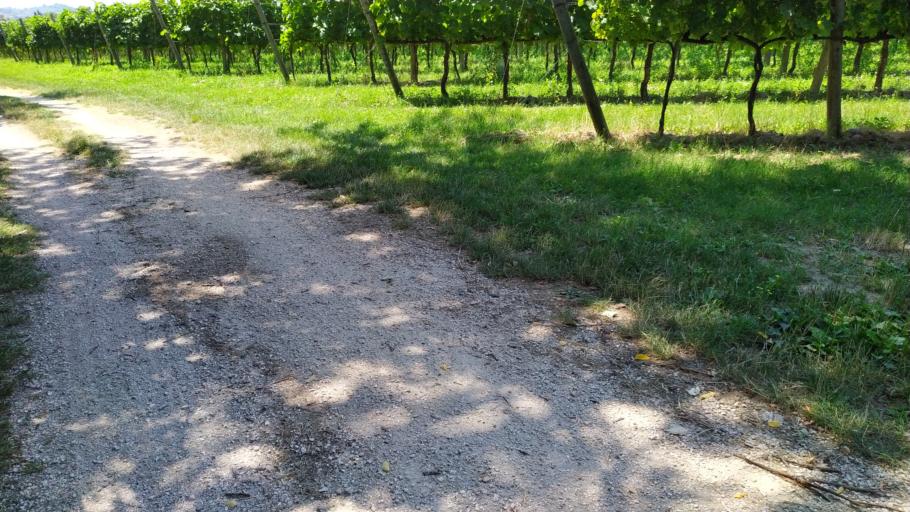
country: IT
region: Emilia-Romagna
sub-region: Forli-Cesena
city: Castrocaro Terme e Terra del Sole
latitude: 44.1967
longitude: 11.9785
